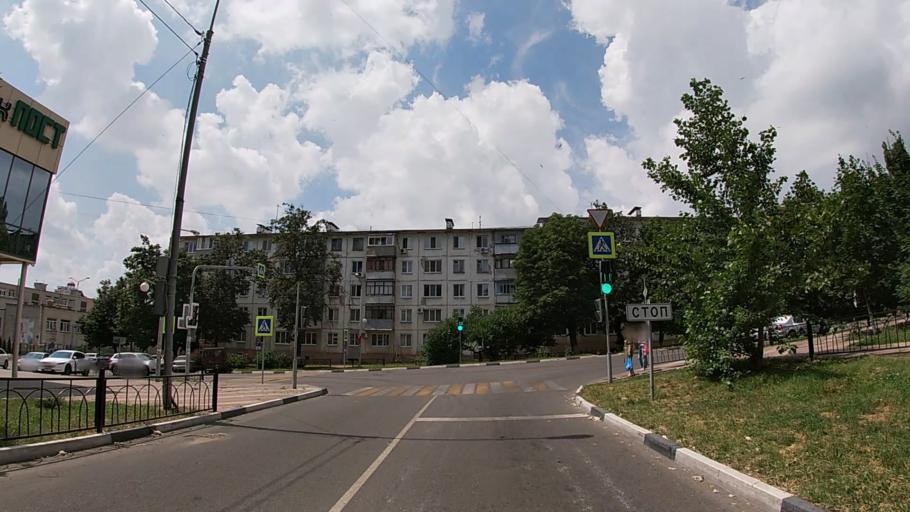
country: RU
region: Belgorod
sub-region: Belgorodskiy Rayon
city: Belgorod
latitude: 50.6046
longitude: 36.5961
